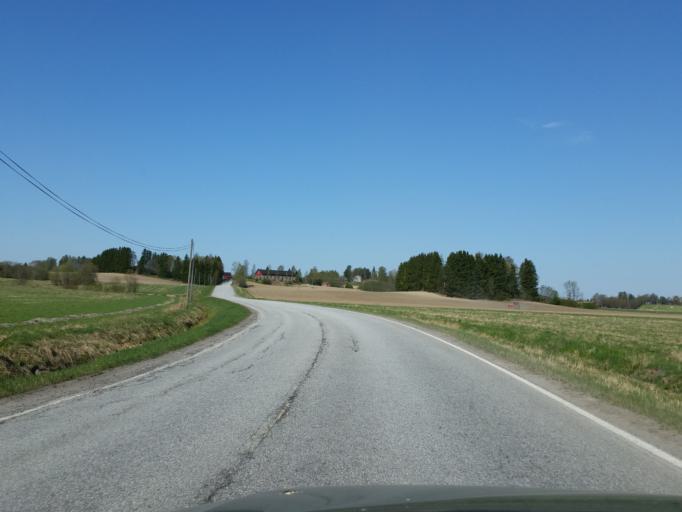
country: FI
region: Uusimaa
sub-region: Helsinki
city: Siuntio
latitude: 60.1752
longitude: 24.1552
